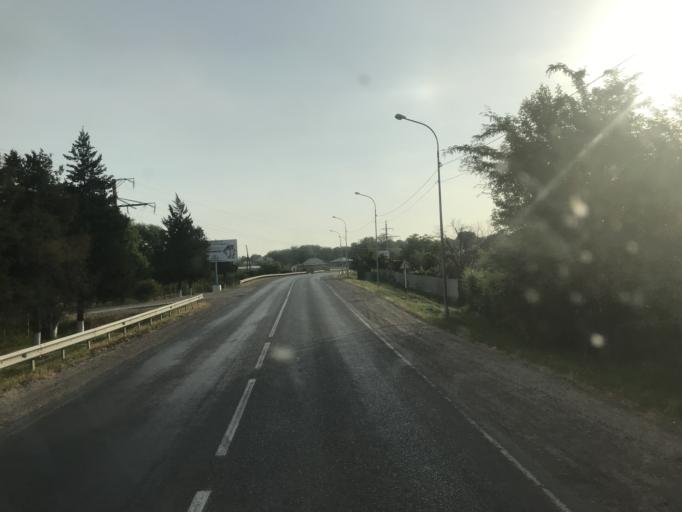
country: KZ
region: Ongtustik Qazaqstan
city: Saryaghash
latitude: 41.4884
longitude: 69.2585
